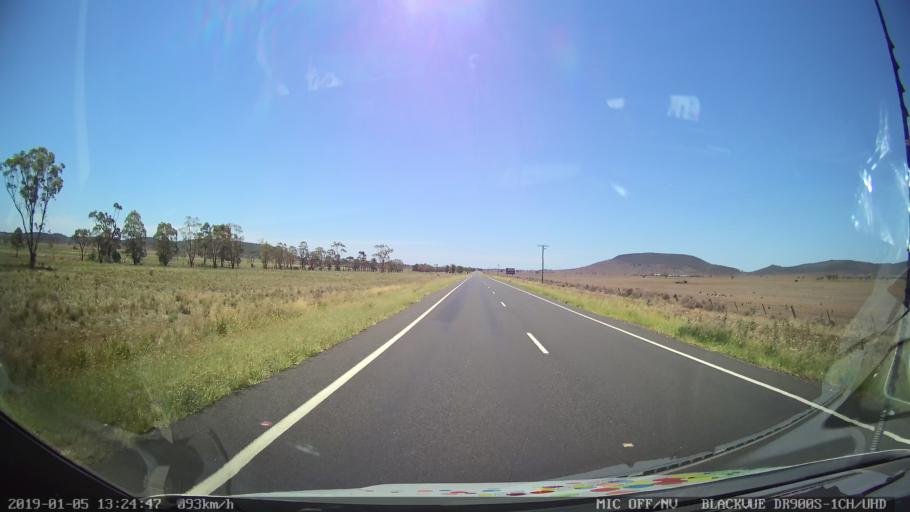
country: AU
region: New South Wales
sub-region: Gunnedah
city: Gunnedah
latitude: -31.0666
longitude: 149.9937
